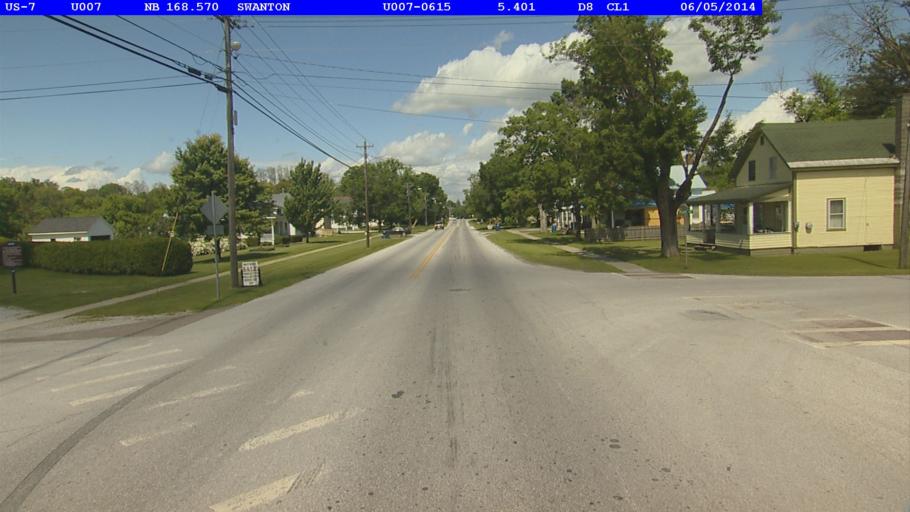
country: US
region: Vermont
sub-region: Franklin County
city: Swanton
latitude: 44.9151
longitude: -73.1182
